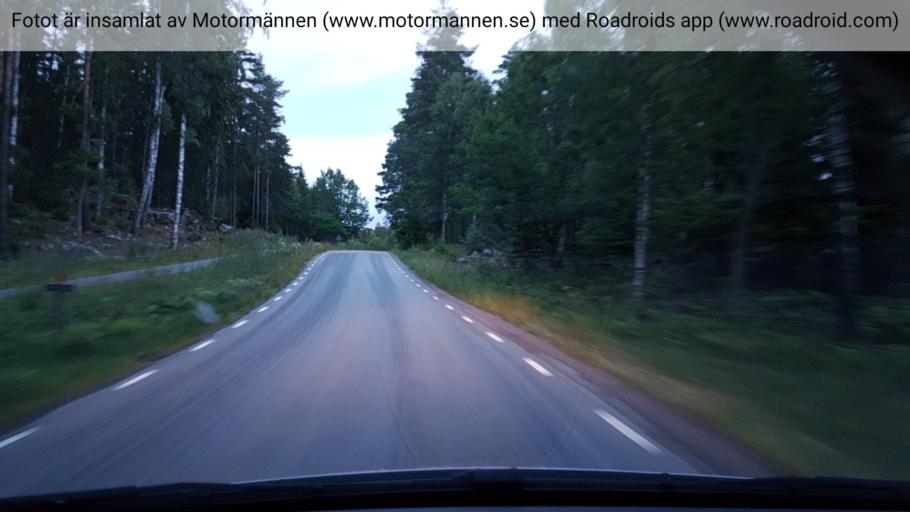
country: SE
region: Vaestmanland
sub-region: Vasteras
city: Vasteras
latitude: 59.5628
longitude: 16.6609
